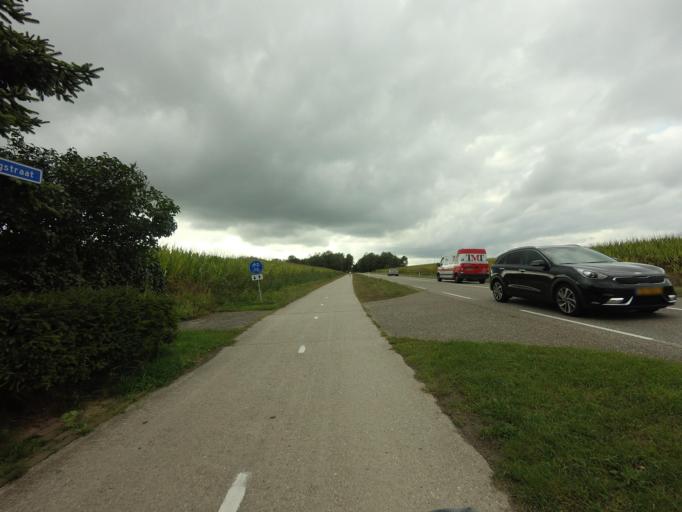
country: NL
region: Overijssel
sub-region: Gemeente Losser
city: Losser
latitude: 52.2350
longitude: 6.9982
